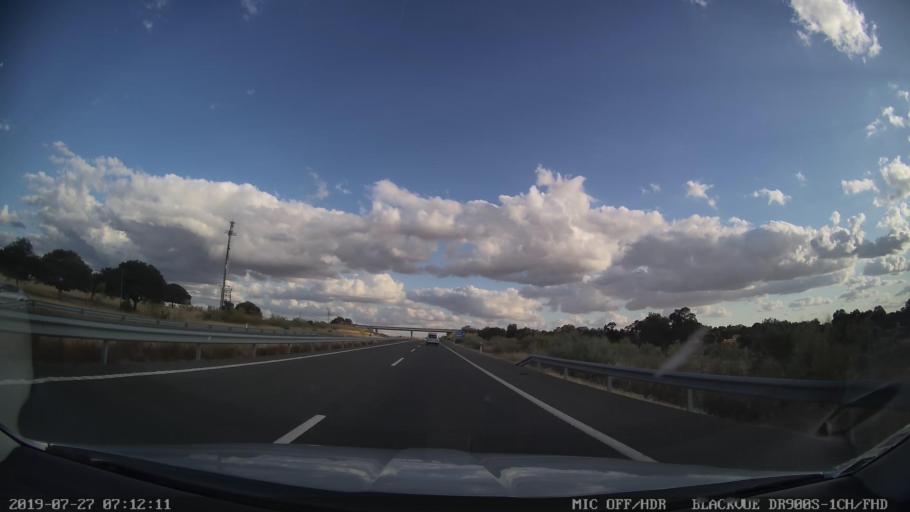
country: ES
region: Extremadura
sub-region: Provincia de Caceres
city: Trujillo
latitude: 39.5370
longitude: -5.8335
